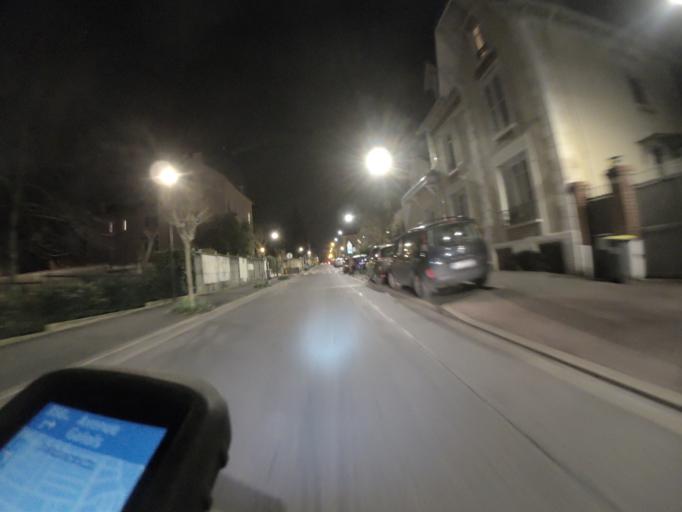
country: FR
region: Ile-de-France
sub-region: Departement des Hauts-de-Seine
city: Bourg-la-Reine
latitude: 48.7796
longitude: 2.3200
